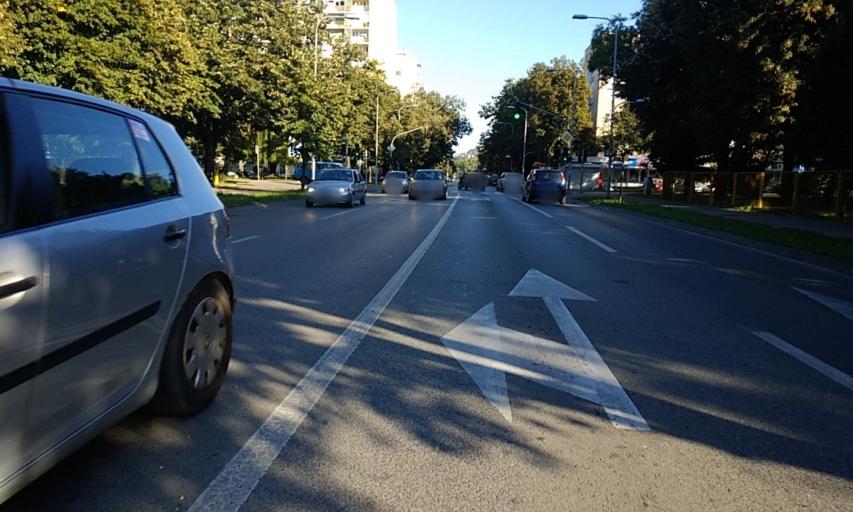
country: BA
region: Republika Srpska
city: Banja Luka
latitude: 44.7702
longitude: 17.1841
